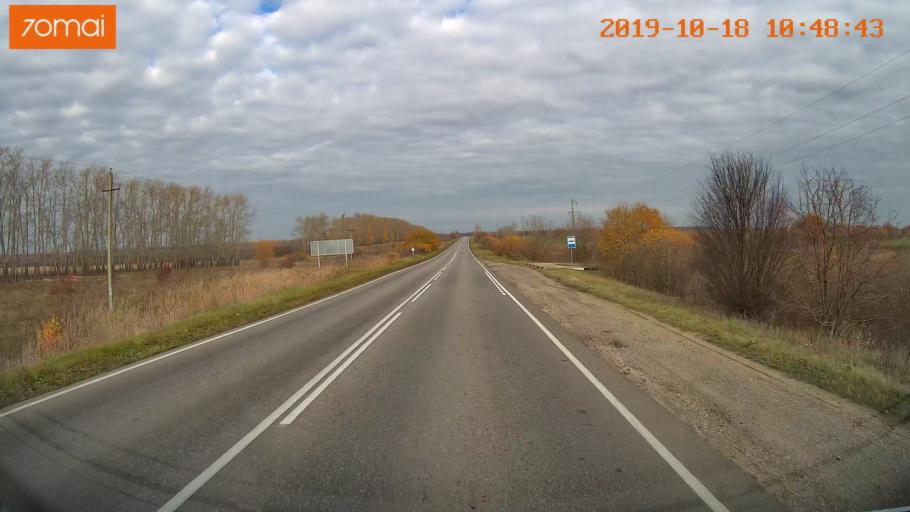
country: RU
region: Tula
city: Yepifan'
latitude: 53.7209
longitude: 38.6972
